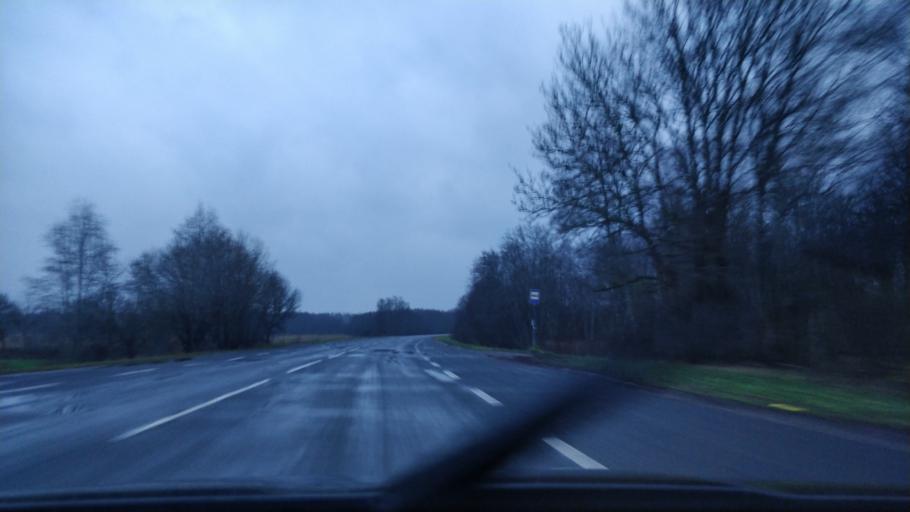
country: EE
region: Laeaene
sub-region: Lihula vald
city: Lihula
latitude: 58.7060
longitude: 23.8624
